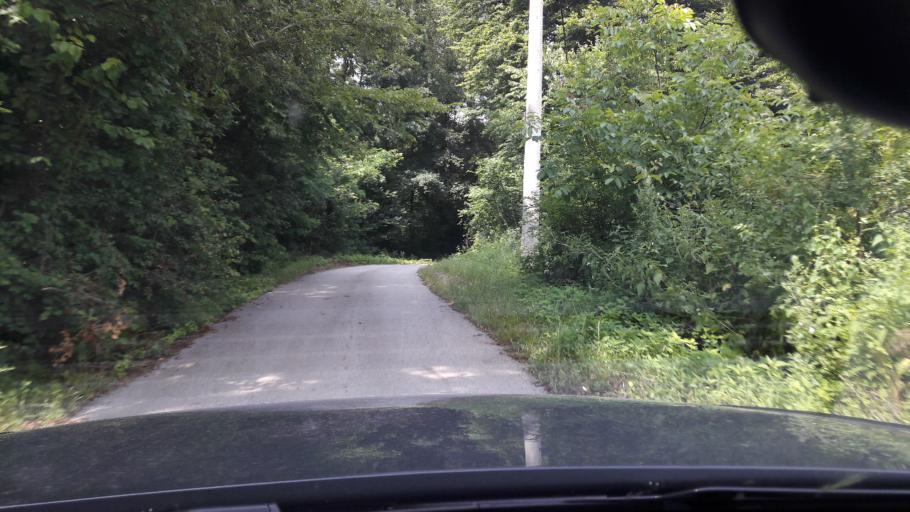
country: RS
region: Central Serbia
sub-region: Belgrade
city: Sopot
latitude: 44.6246
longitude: 20.5994
